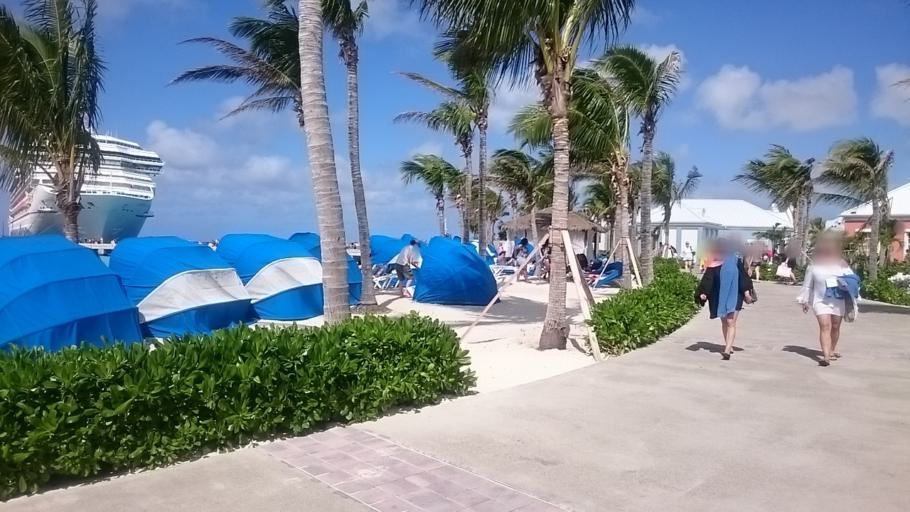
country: TC
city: Cockburn Town
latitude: 21.4263
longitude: -71.1447
